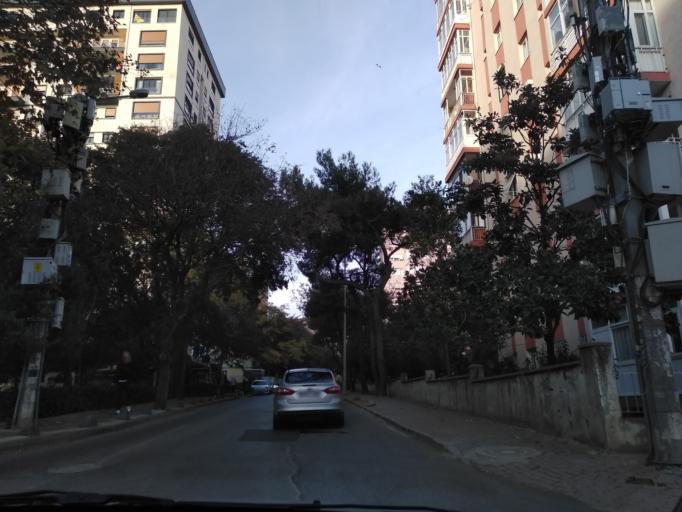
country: TR
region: Istanbul
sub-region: Atasehir
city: Atasehir
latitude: 40.9710
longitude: 29.0907
